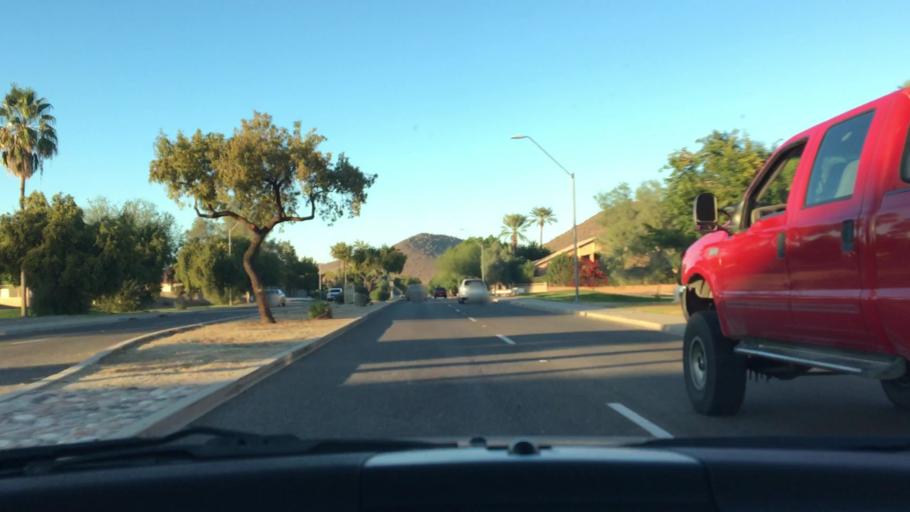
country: US
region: Arizona
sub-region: Maricopa County
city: Peoria
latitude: 33.6762
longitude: -112.1867
